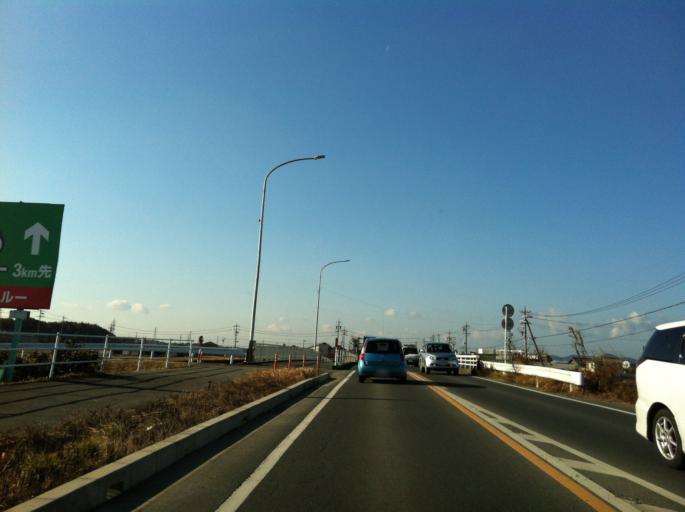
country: JP
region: Aichi
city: Tahara
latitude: 34.6913
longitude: 137.3278
